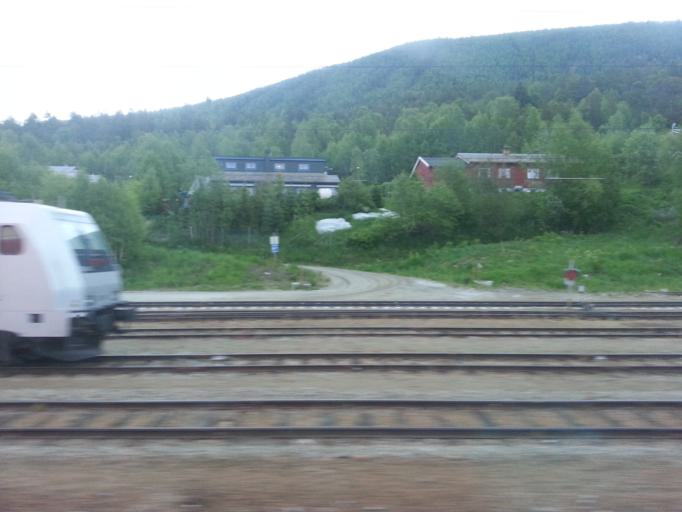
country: NO
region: Oppland
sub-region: Dovre
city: Dombas
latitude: 62.0681
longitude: 9.1256
